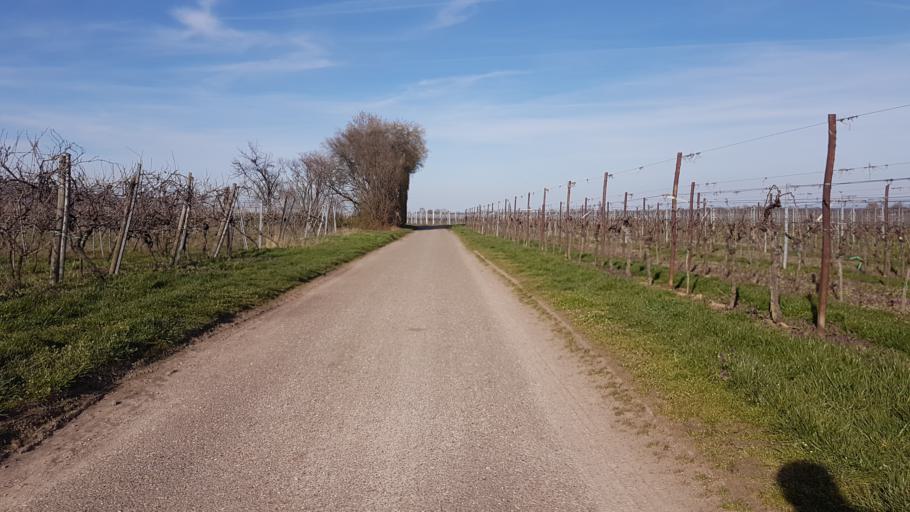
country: DE
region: Rheinland-Pfalz
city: Kirrweiler
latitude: 49.3084
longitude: 8.1509
